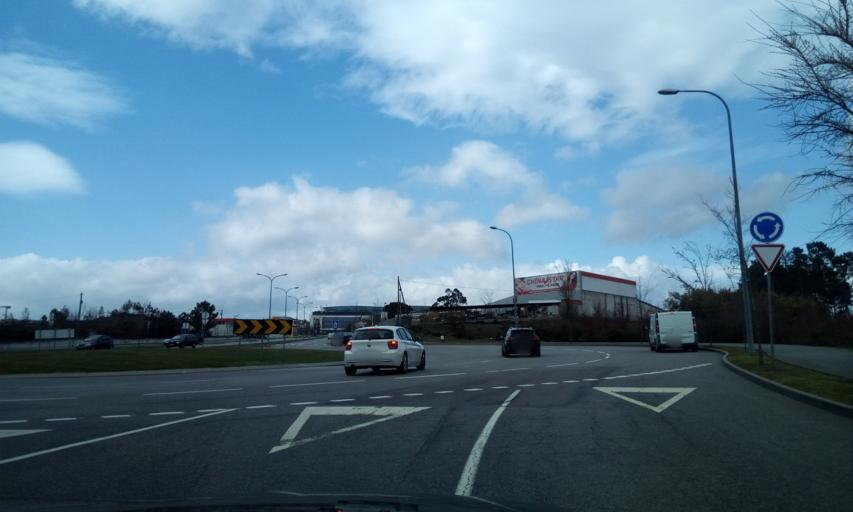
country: PT
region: Viseu
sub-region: Viseu
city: Viseu
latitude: 40.6361
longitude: -7.9071
